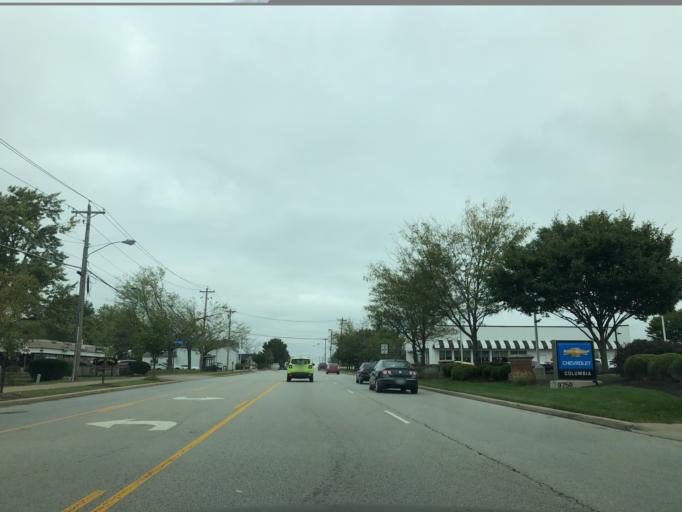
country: US
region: Ohio
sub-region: Hamilton County
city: Montgomery
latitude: 39.2328
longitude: -84.3519
